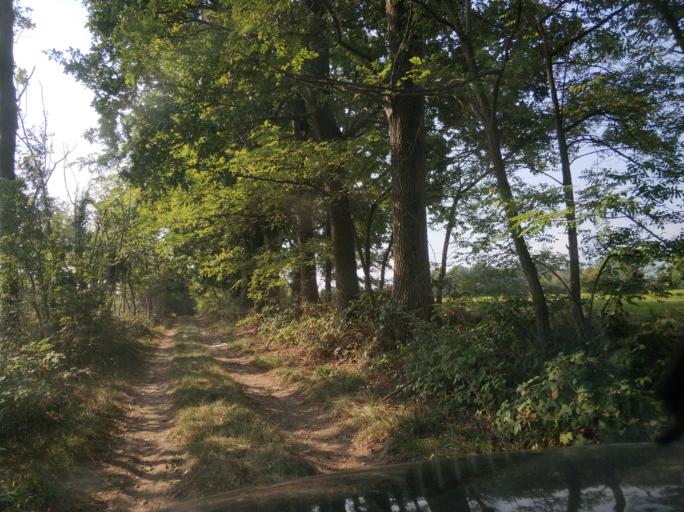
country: IT
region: Piedmont
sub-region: Provincia di Torino
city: San Carlo Canavese
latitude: 45.2615
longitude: 7.5882
